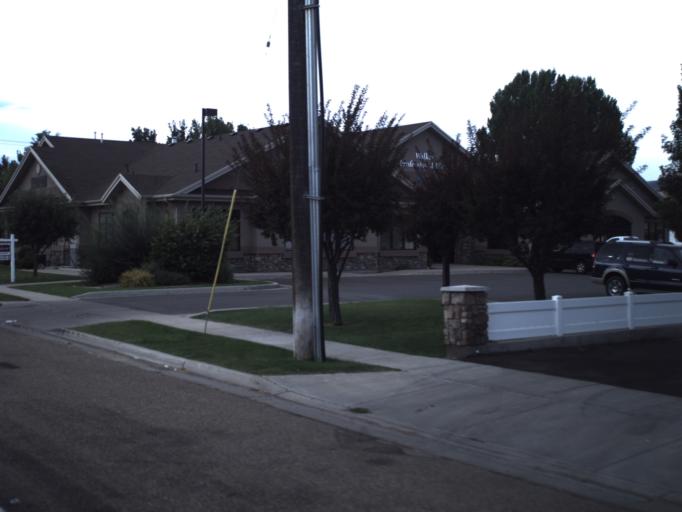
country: US
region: Utah
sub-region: Morgan County
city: Morgan
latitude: 41.0402
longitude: -111.6795
